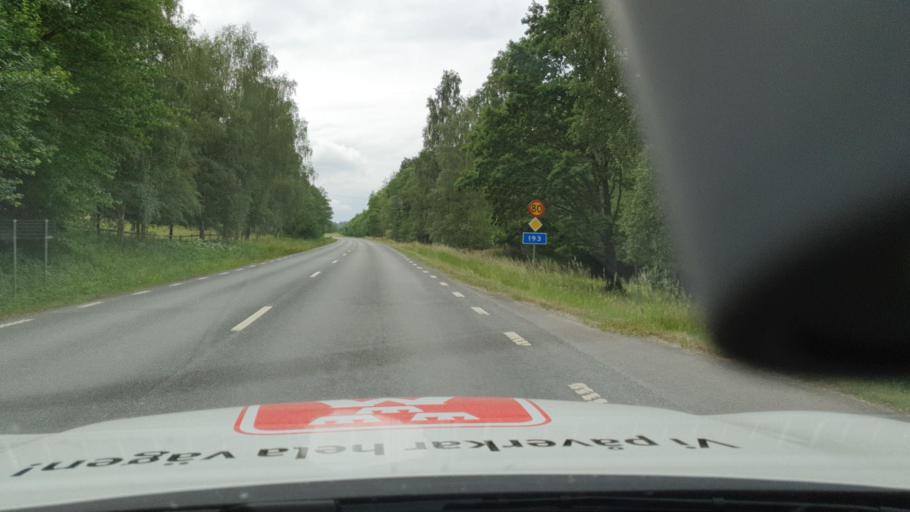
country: SE
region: Vaestra Goetaland
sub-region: Hjo Kommun
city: Hjo
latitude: 58.2262
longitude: 14.2057
